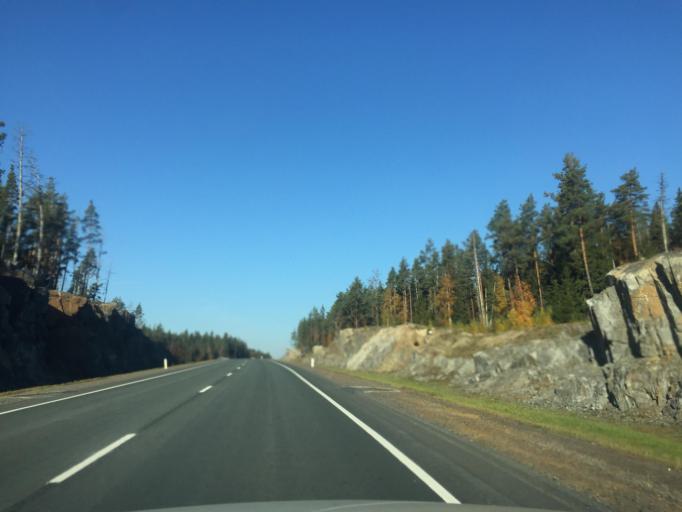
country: RU
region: Leningrad
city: Kuznechnoye
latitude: 61.1843
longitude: 29.8170
